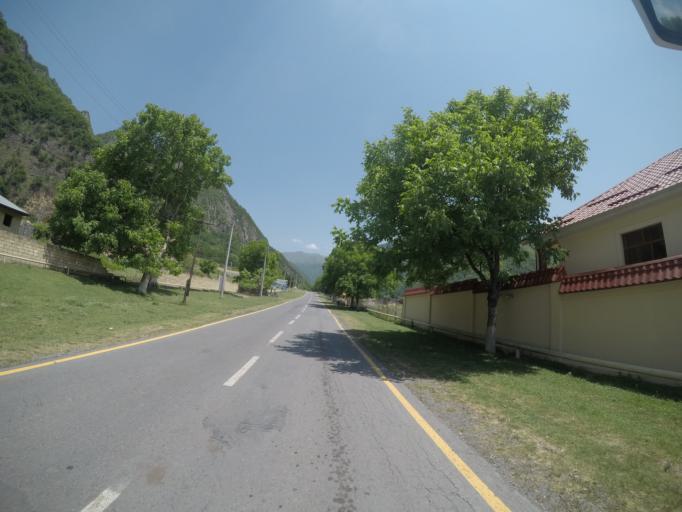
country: AZ
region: Qakh Rayon
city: Qaxbas
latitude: 41.4526
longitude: 47.0104
